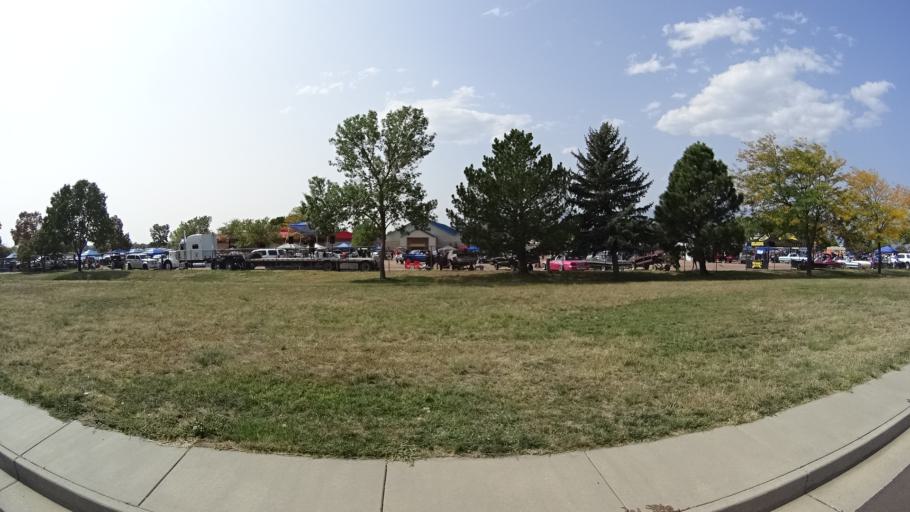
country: US
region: Colorado
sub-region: El Paso County
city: Cimarron Hills
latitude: 38.8386
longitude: -104.7312
